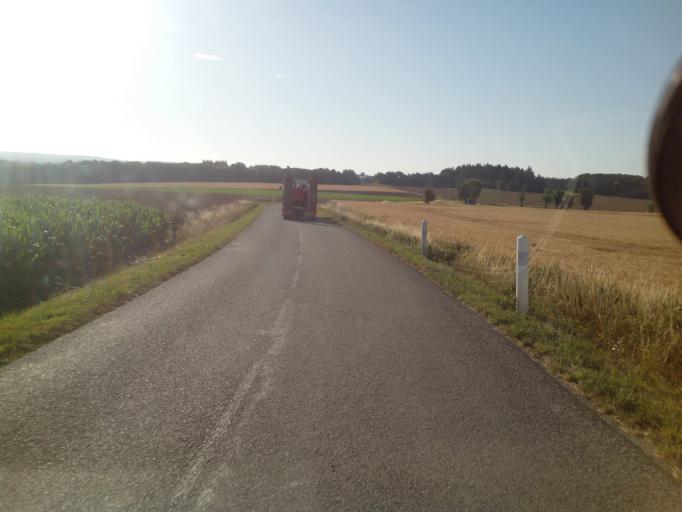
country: FR
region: Brittany
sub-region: Departement du Morbihan
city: Loyat
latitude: 48.0128
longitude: -2.3981
